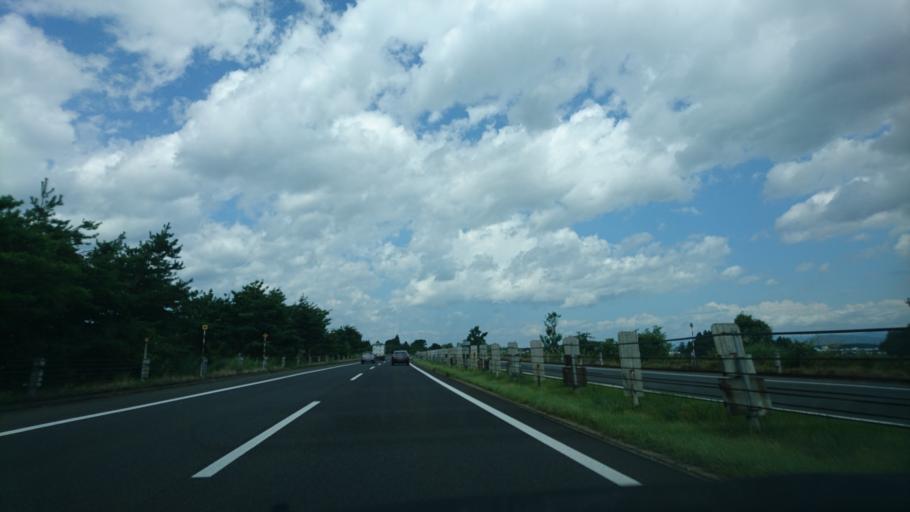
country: JP
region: Iwate
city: Morioka-shi
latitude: 39.5859
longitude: 141.1180
